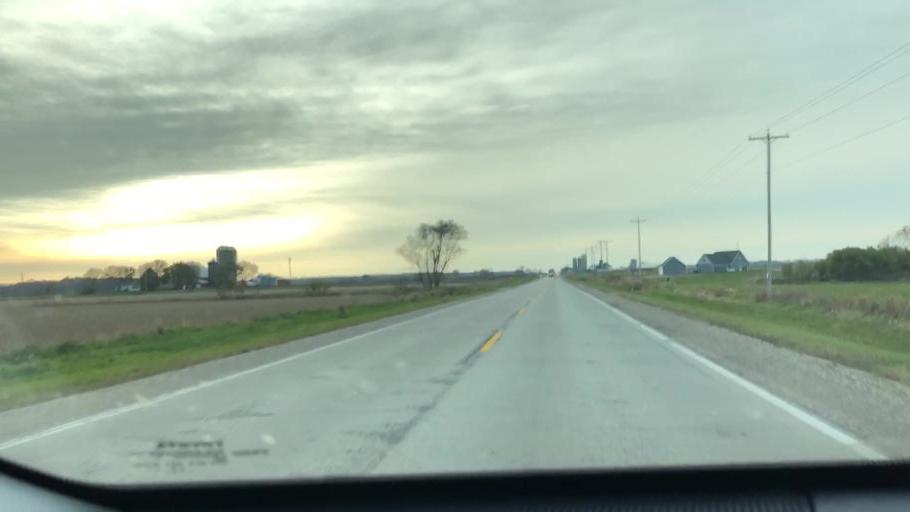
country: US
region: Wisconsin
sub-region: Outagamie County
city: Seymour
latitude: 44.4439
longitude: -88.2866
